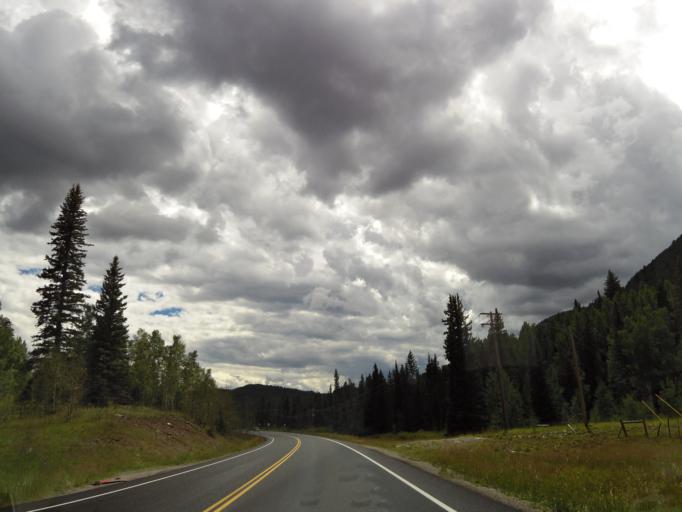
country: US
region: Colorado
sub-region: San Juan County
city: Silverton
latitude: 37.6442
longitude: -107.8071
